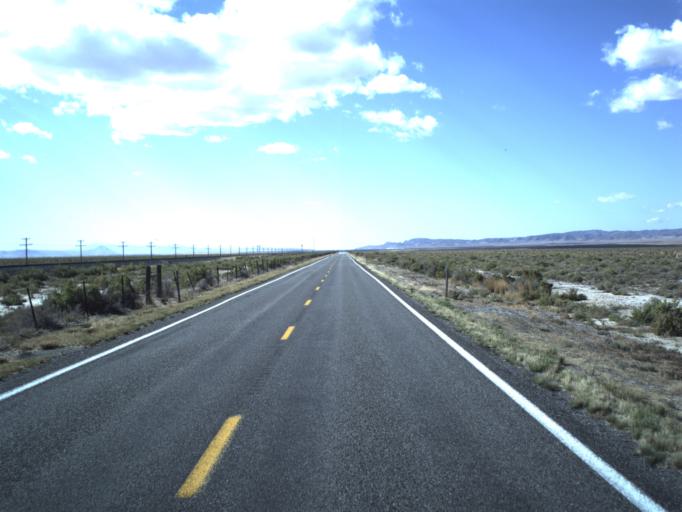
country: US
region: Utah
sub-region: Millard County
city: Delta
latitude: 39.0871
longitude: -112.7528
